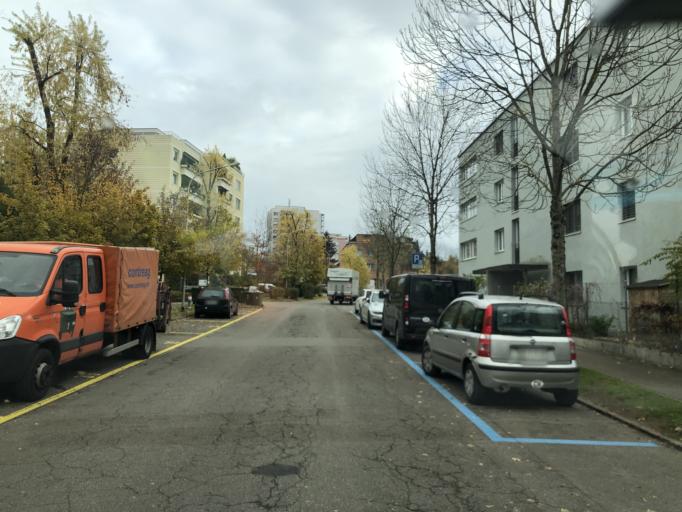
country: CH
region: Aargau
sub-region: Bezirk Baden
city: Neuenhof
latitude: 47.4594
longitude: 8.3318
